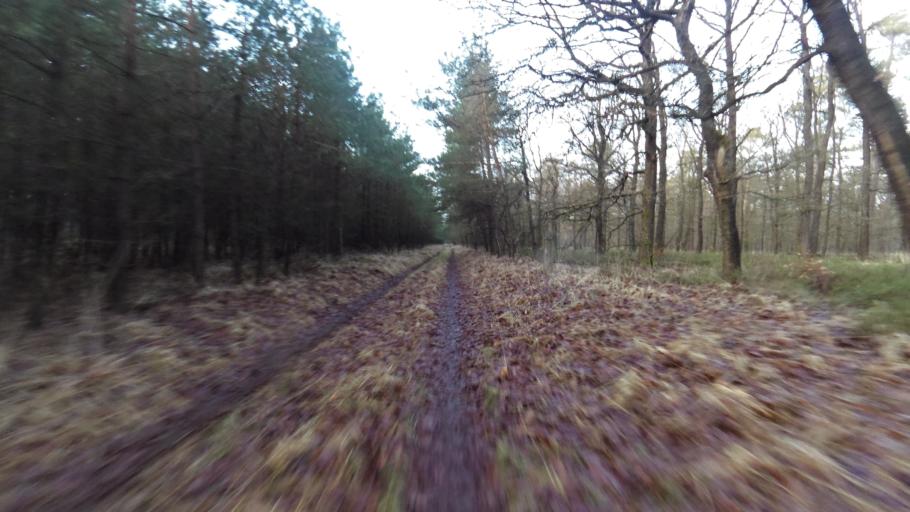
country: NL
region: Gelderland
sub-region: Gemeente Apeldoorn
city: Uddel
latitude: 52.2965
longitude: 5.8432
